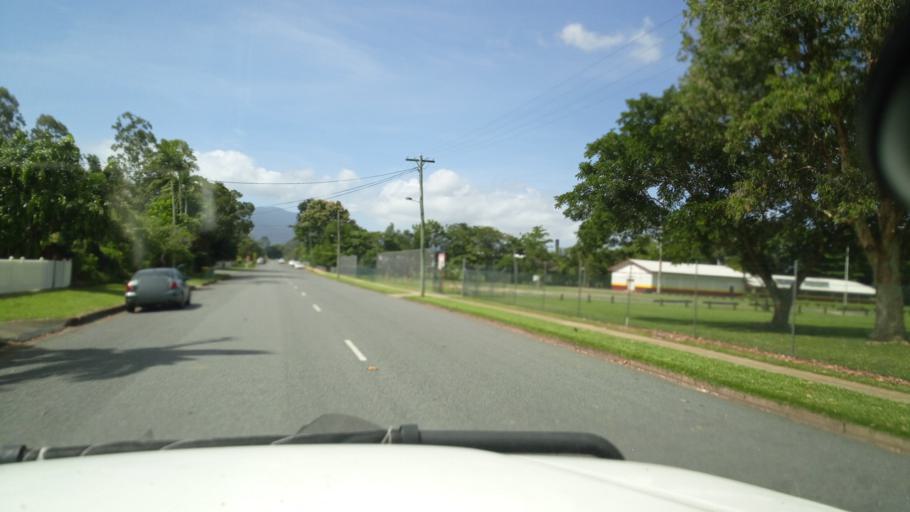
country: AU
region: Queensland
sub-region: Cairns
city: Woree
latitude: -17.0890
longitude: 145.7817
